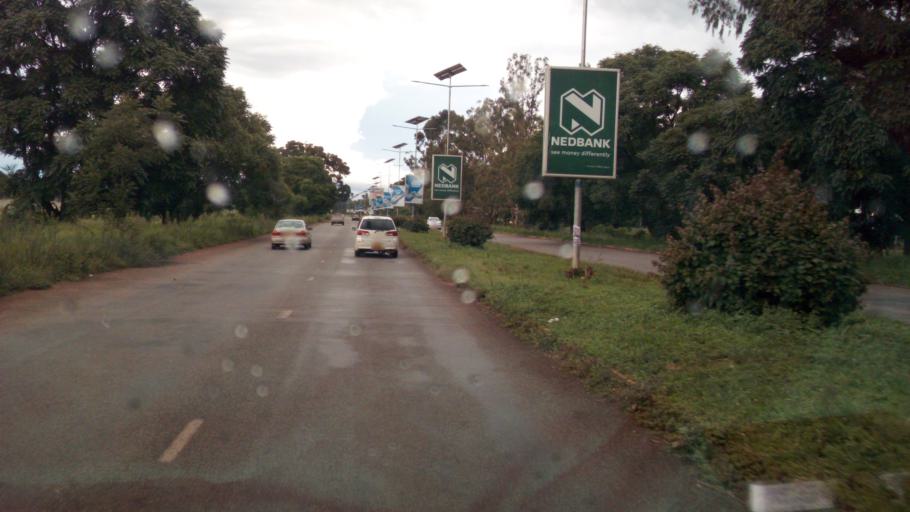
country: ZW
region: Harare
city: Harare
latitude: -17.7817
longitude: 31.0813
